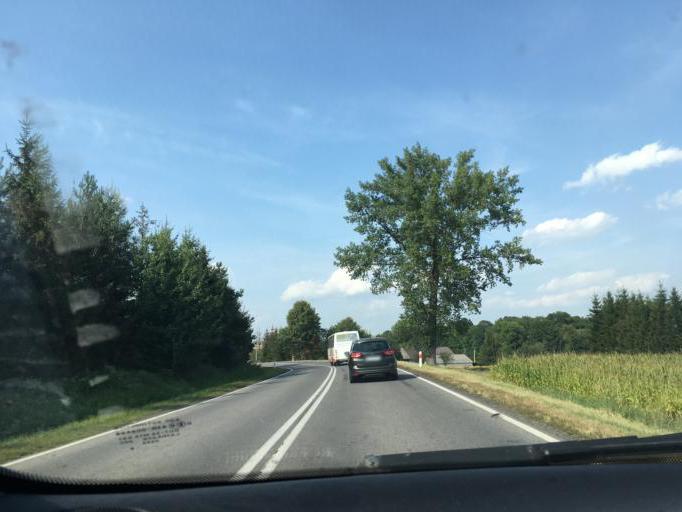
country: PL
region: Opole Voivodeship
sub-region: Powiat prudnicki
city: Laka Prudnicka
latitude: 50.3713
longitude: 17.5361
